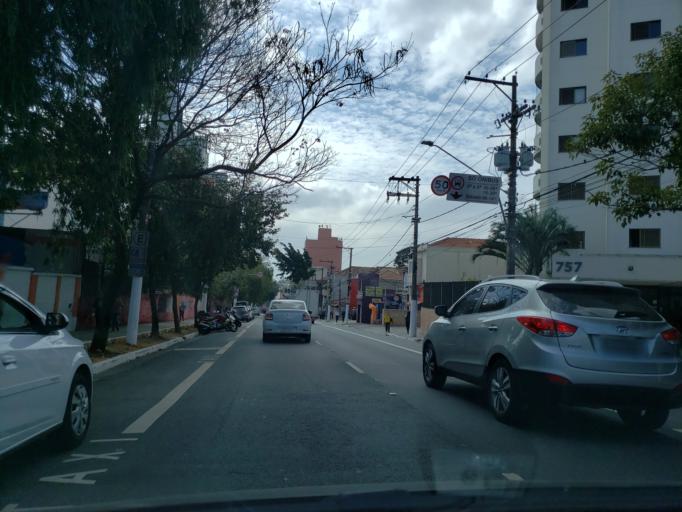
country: BR
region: Sao Paulo
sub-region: Sao Paulo
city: Sao Paulo
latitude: -23.5704
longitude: -46.6223
